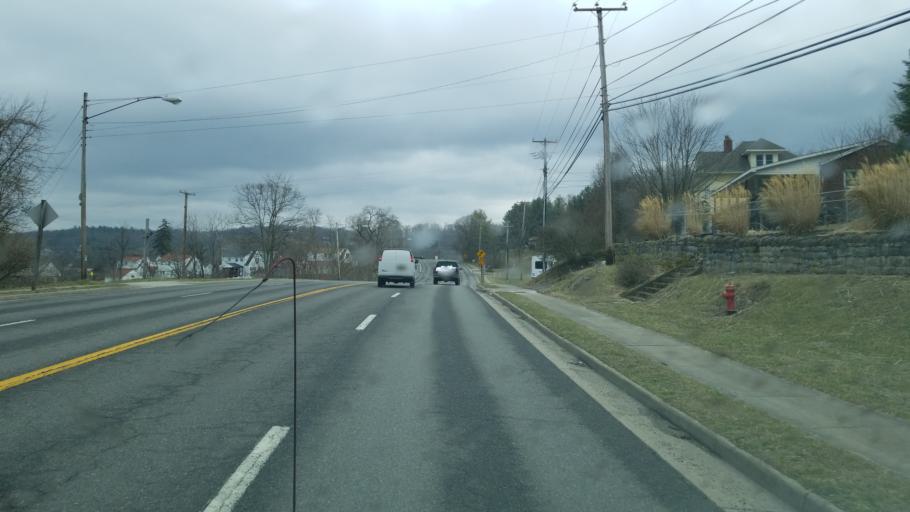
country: US
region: Virginia
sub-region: Giles County
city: Pearisburg
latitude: 37.3234
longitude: -80.7328
